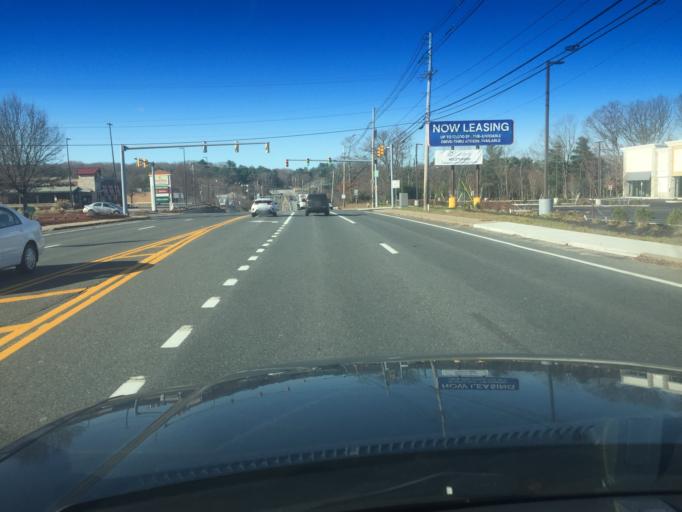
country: US
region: Rhode Island
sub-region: Providence County
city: Greenville
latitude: 41.8703
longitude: -71.5318
